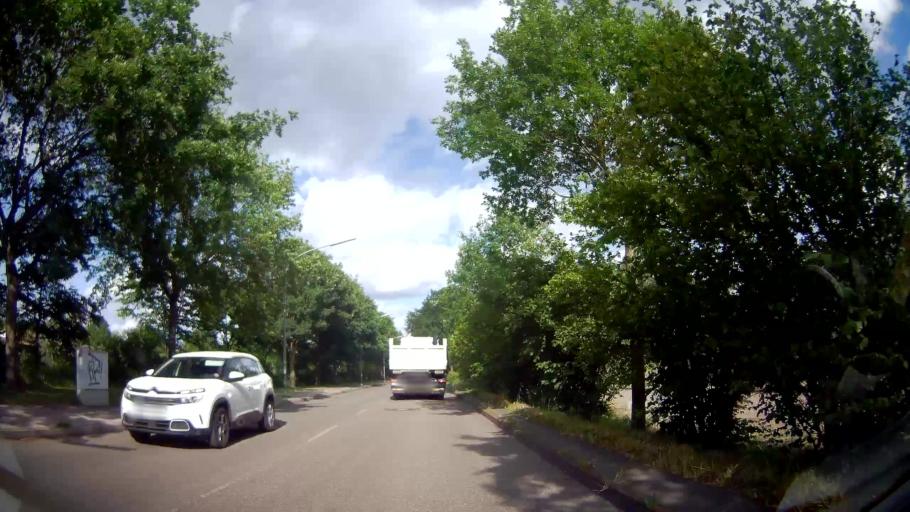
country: DE
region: North Rhine-Westphalia
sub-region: Regierungsbezirk Munster
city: Gelsenkirchen
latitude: 51.5139
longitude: 7.0597
